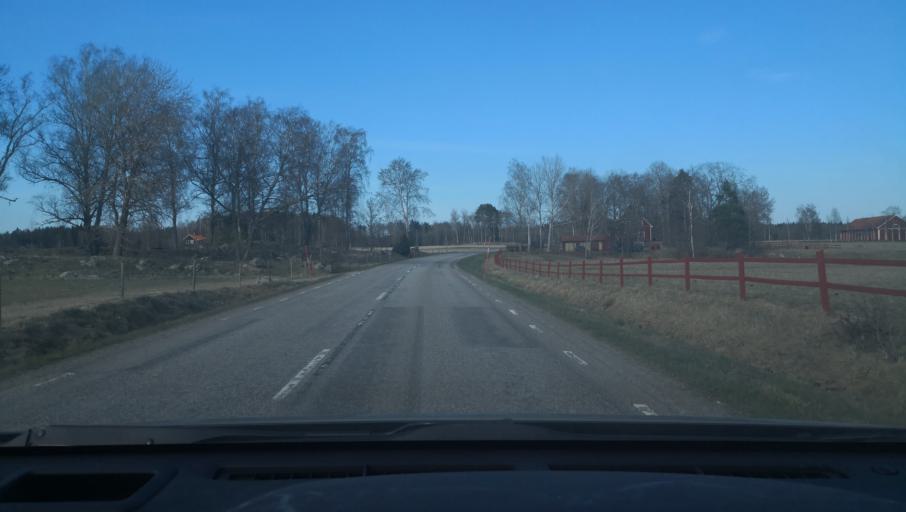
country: SE
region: Uppsala
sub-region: Heby Kommun
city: Heby
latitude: 59.9595
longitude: 16.8847
